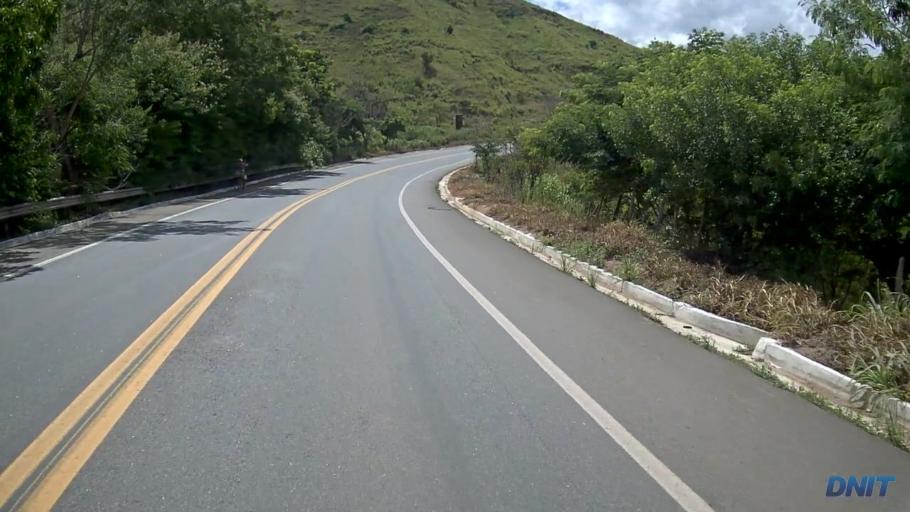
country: BR
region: Minas Gerais
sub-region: Governador Valadares
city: Governador Valadares
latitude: -18.9224
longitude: -42.0272
